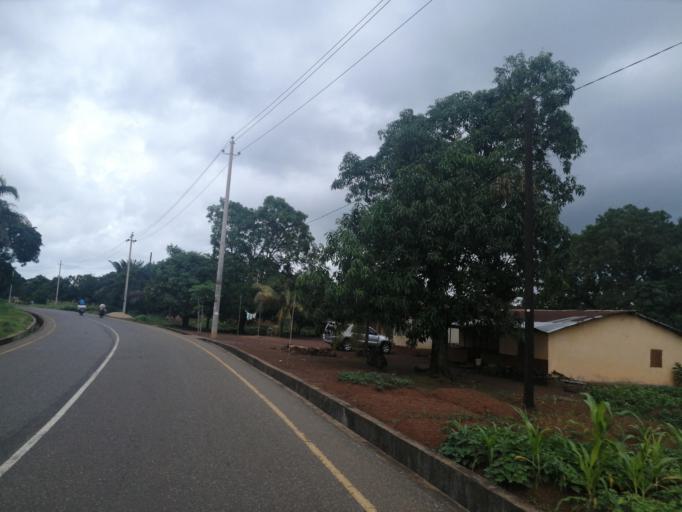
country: SL
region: Northern Province
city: Port Loko
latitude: 8.7499
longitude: -12.7810
